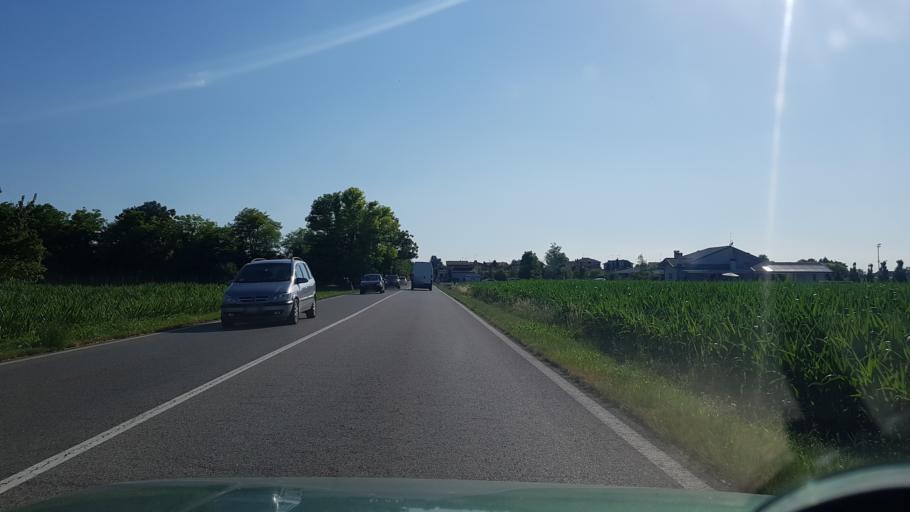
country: IT
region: Friuli Venezia Giulia
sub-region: Provincia di Udine
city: Ruda
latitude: 45.8437
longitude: 13.4028
